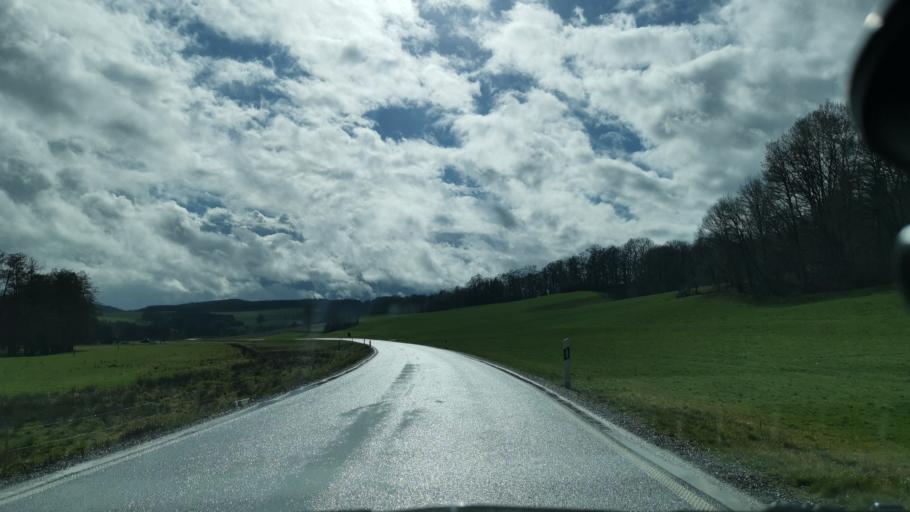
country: DE
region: Hesse
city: Waldkappel
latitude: 51.1412
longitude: 9.8645
